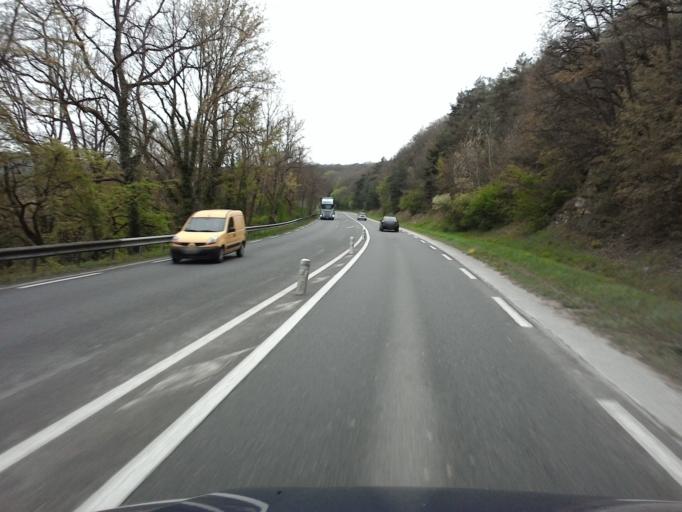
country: FR
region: Champagne-Ardenne
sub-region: Departement de la Haute-Marne
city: Froncles
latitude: 48.2859
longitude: 5.1179
